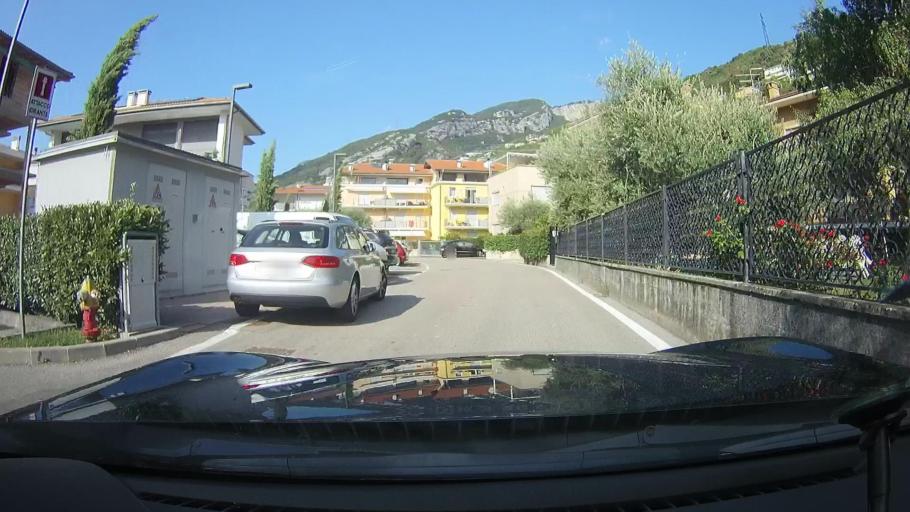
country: IT
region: Trentino-Alto Adige
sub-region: Provincia di Trento
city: Torbole sul Garda
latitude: 45.8733
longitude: 10.8779
